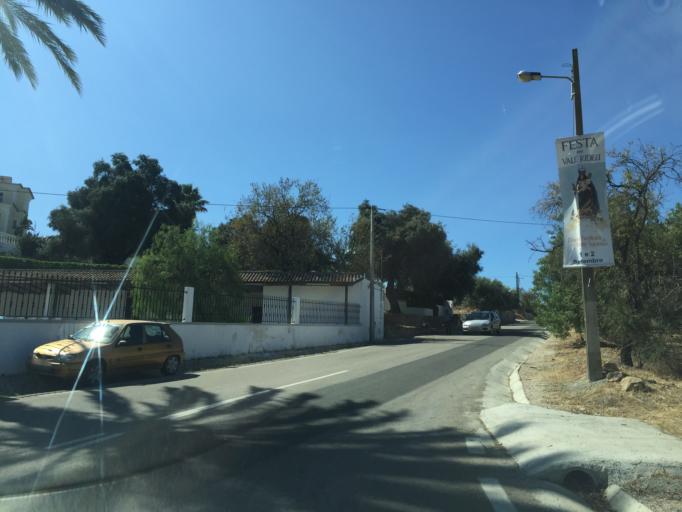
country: PT
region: Faro
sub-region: Loule
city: Vilamoura
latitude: 37.1194
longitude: -8.0984
